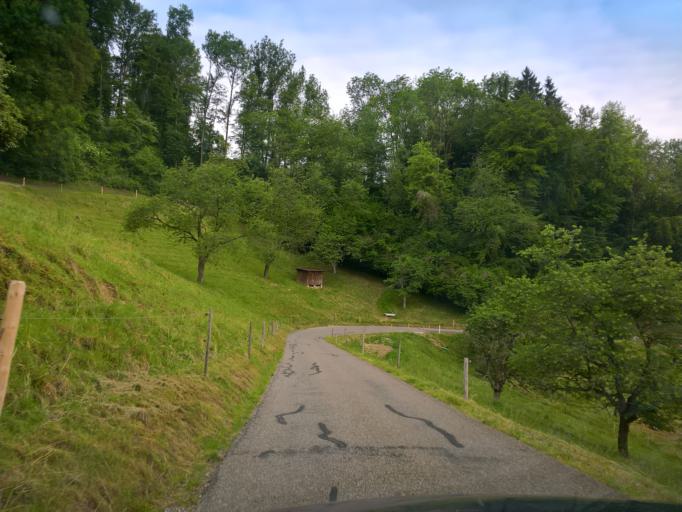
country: CH
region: Zurich
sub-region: Bezirk Buelach
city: Rorbas
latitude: 47.5318
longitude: 8.5677
